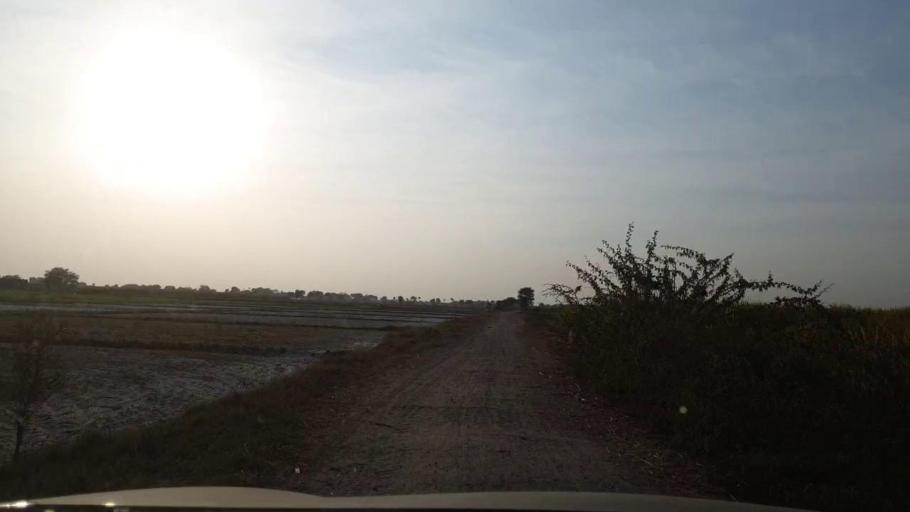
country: PK
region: Sindh
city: Berani
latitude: 25.7067
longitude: 68.7454
